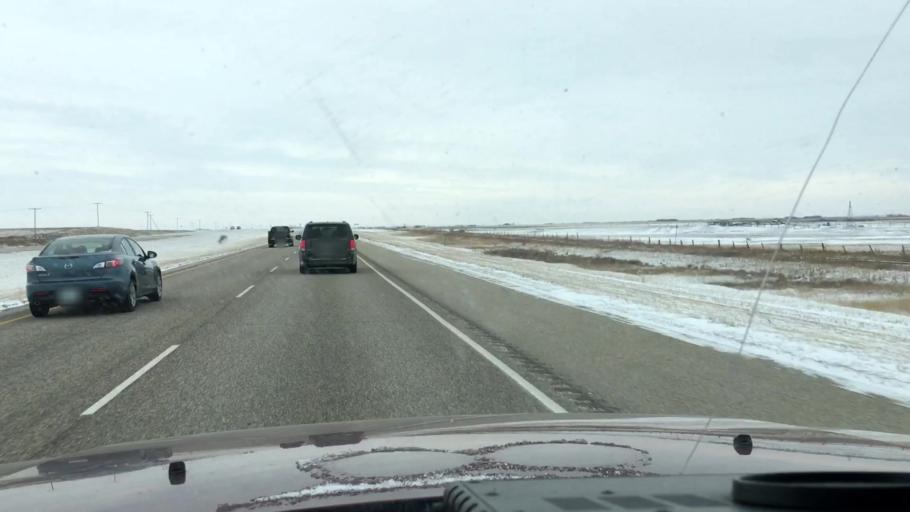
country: CA
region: Saskatchewan
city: Saskatoon
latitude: 51.5947
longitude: -106.3870
